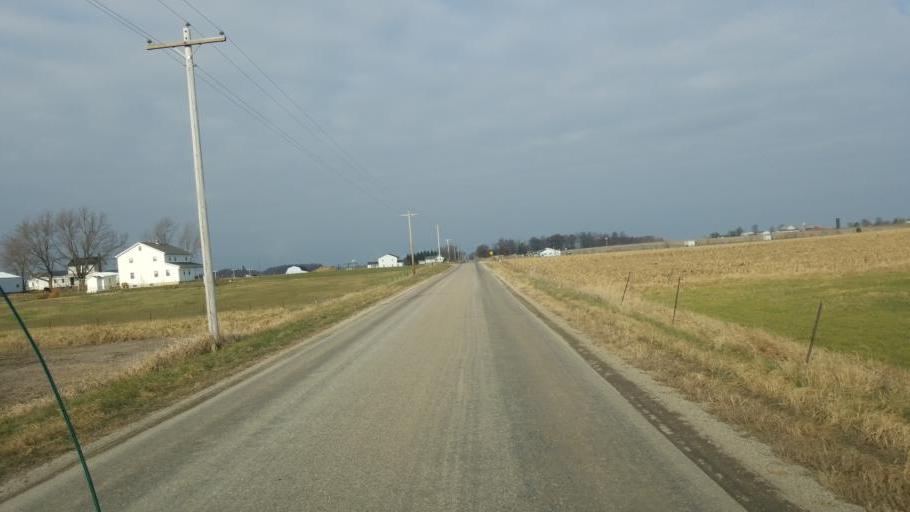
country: US
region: Indiana
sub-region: Adams County
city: Berne
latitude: 40.6323
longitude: -84.9356
